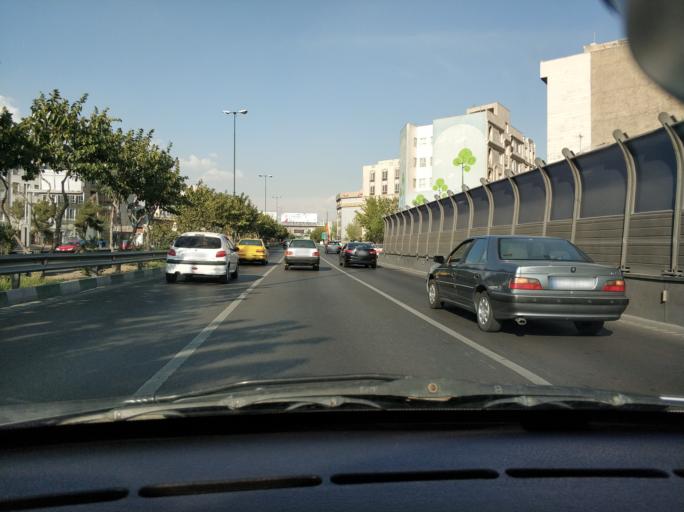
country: IR
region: Tehran
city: Tehran
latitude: 35.7218
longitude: 51.3614
